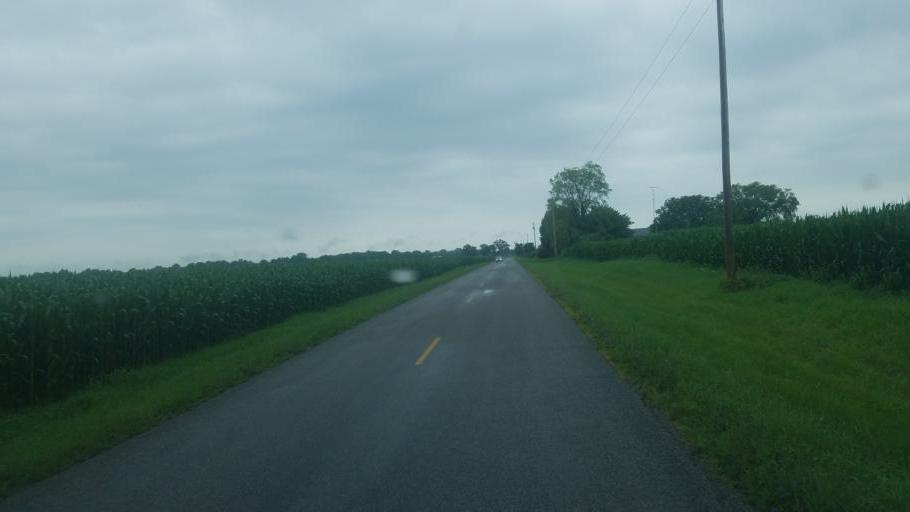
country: US
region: Ohio
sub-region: Union County
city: Richwood
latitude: 40.5118
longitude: -83.4660
